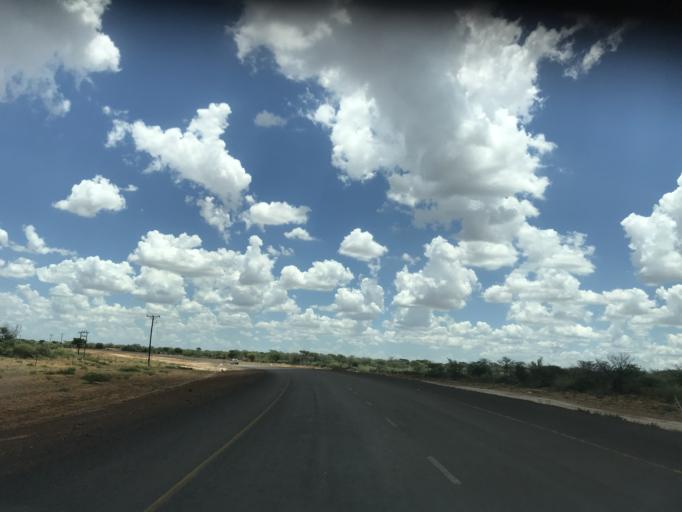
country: BW
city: Mabuli
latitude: -25.8010
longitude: 24.7106
